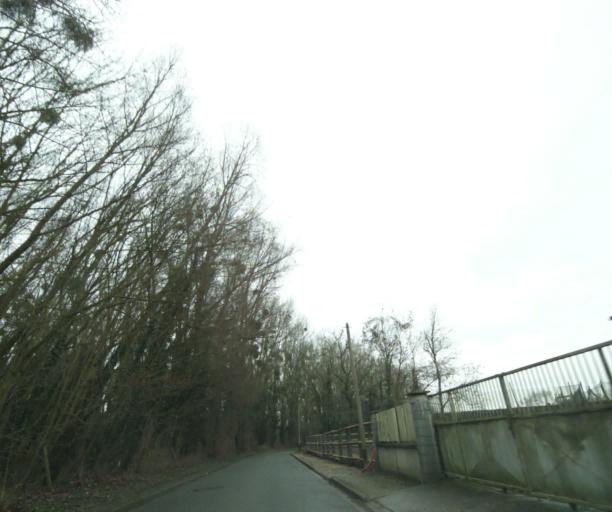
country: FR
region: Ile-de-France
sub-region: Departement de l'Essonne
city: Champlan
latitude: 48.7027
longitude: 2.2709
